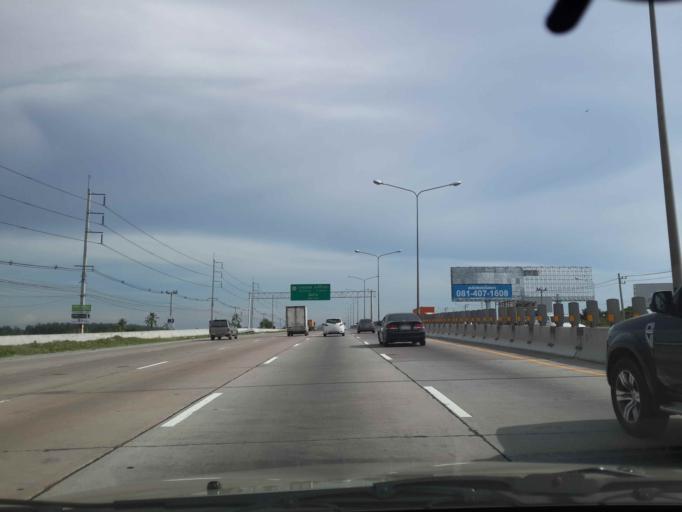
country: TH
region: Chon Buri
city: Si Racha
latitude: 13.1767
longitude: 100.9941
